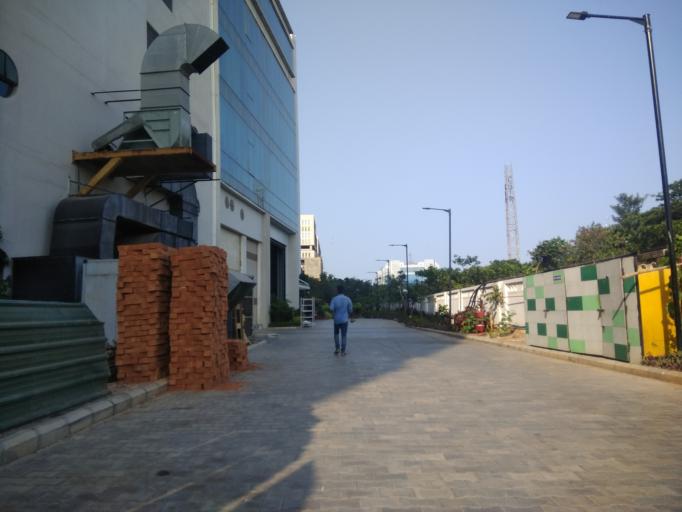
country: IN
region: Tamil Nadu
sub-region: Chennai
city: Gandhi Nagar
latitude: 12.9899
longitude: 80.2428
